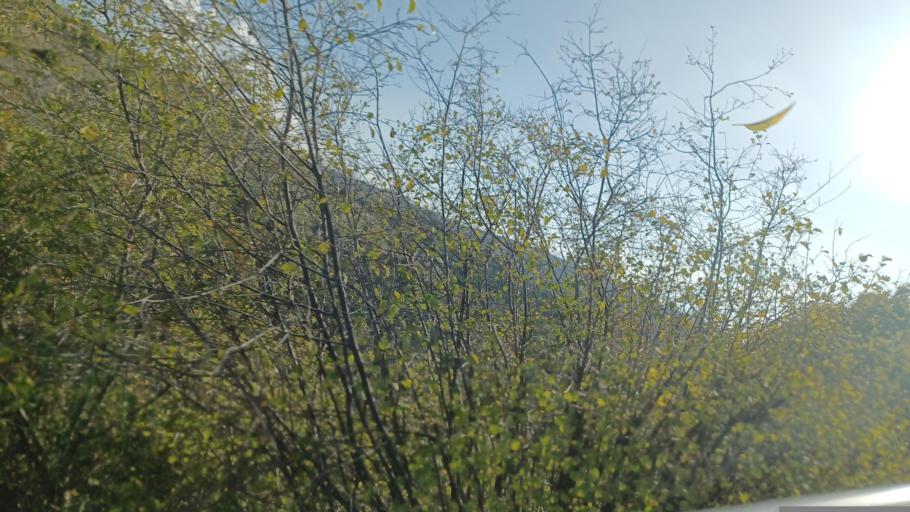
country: CY
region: Pafos
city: Mesogi
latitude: 34.8108
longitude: 32.4904
